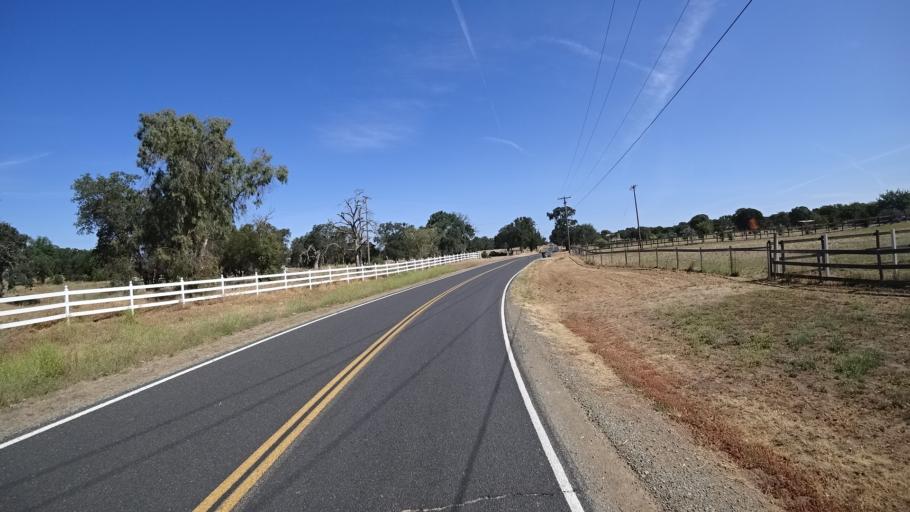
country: US
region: California
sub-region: Calaveras County
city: Rancho Calaveras
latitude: 38.1145
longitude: -120.9268
